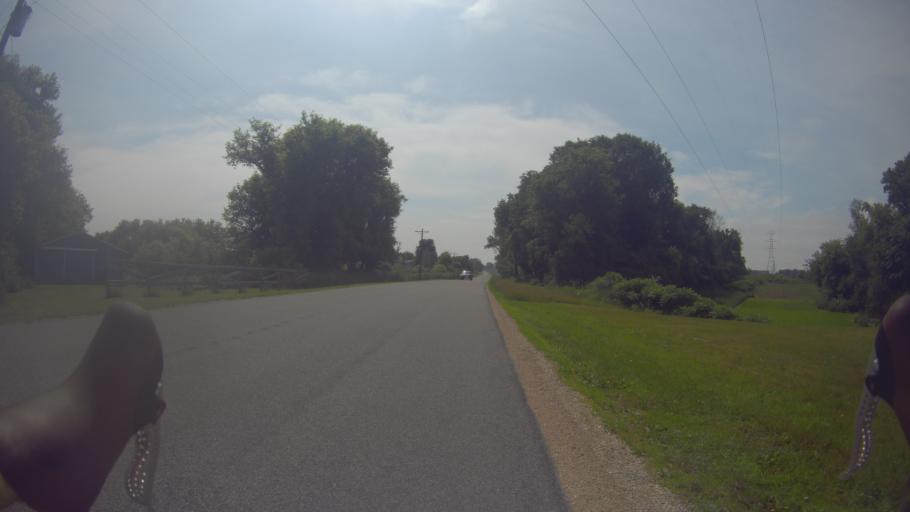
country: US
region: Wisconsin
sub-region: Rock County
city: Edgerton
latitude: 42.8619
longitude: -89.0483
